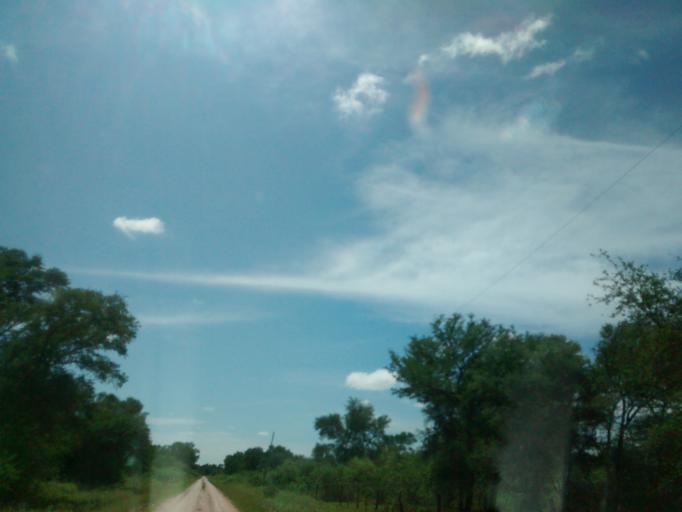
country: AR
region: Chaco
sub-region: Departamento de Quitilipi
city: Quitilipi
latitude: -26.7908
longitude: -60.2025
